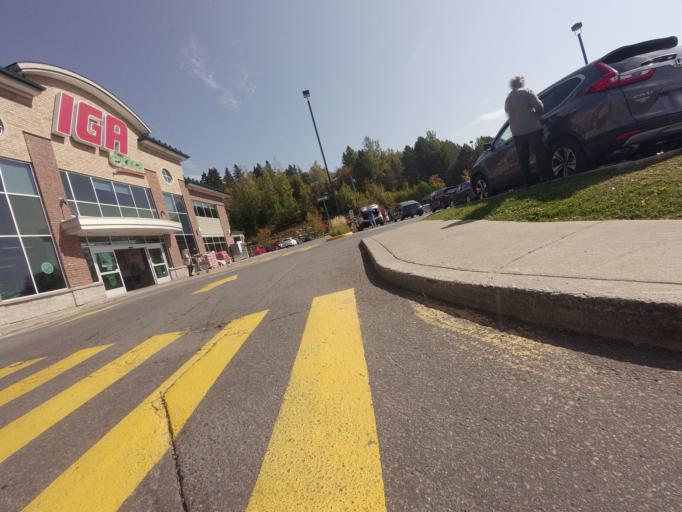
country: CA
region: Quebec
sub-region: Laurentides
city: Sainte-Agathe-des-Monts
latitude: 46.0467
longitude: -74.2780
